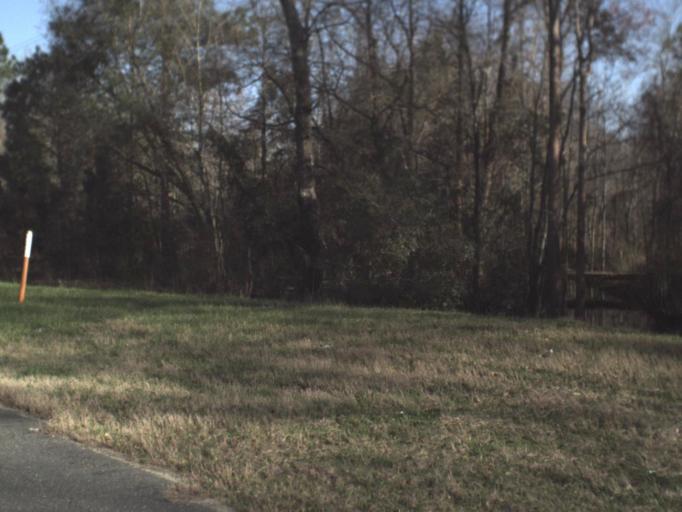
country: US
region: Florida
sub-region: Washington County
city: Chipley
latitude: 30.7873
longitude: -85.4373
